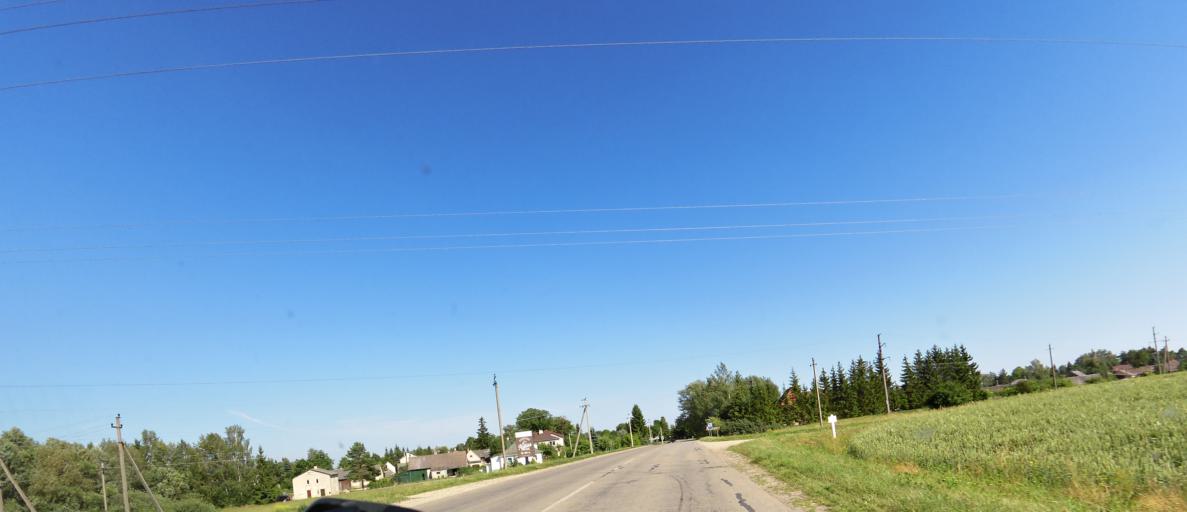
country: LT
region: Panevezys
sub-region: Birzai
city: Birzai
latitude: 56.2060
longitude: 24.7201
